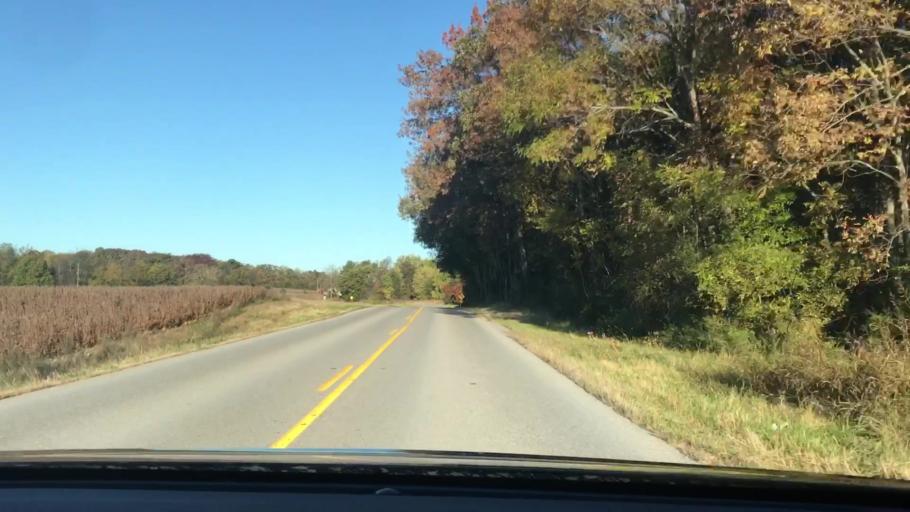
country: US
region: Kentucky
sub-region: Logan County
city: Auburn
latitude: 36.8174
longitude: -86.6446
